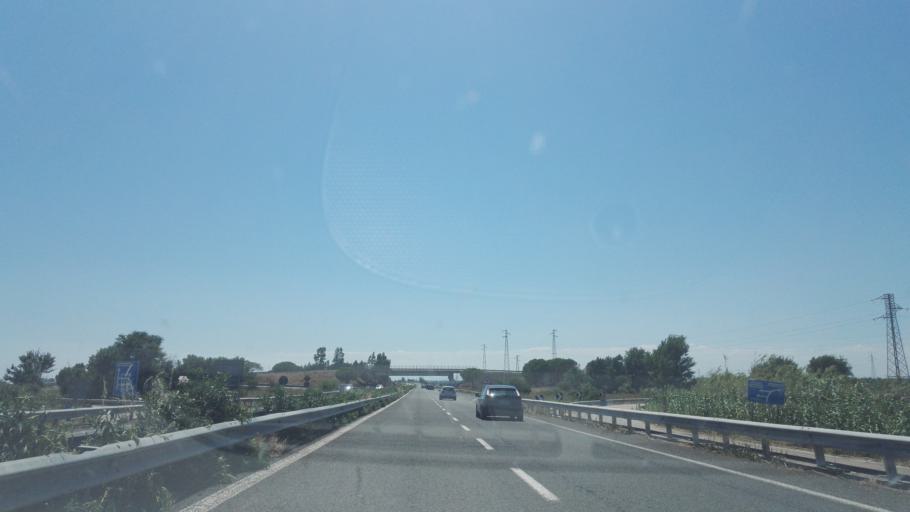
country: IT
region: Apulia
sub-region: Provincia di Taranto
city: Marina di Ginosa
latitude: 40.4353
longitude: 16.8372
